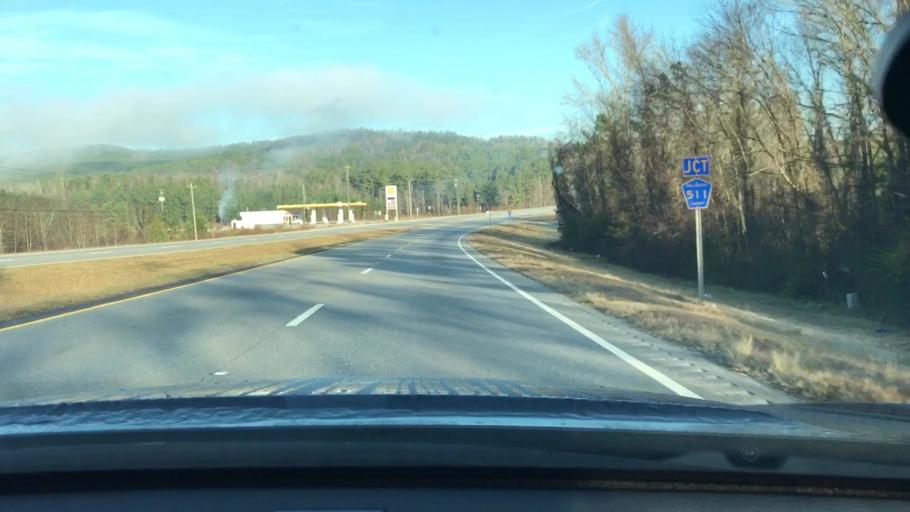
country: US
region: Alabama
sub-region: Talladega County
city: Mignon
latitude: 33.1912
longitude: -86.3066
